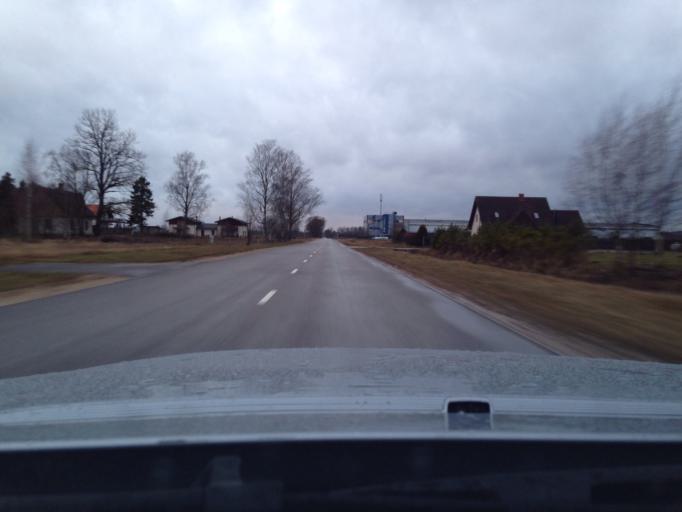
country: LV
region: Marupe
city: Marupe
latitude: 56.8845
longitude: 24.0030
